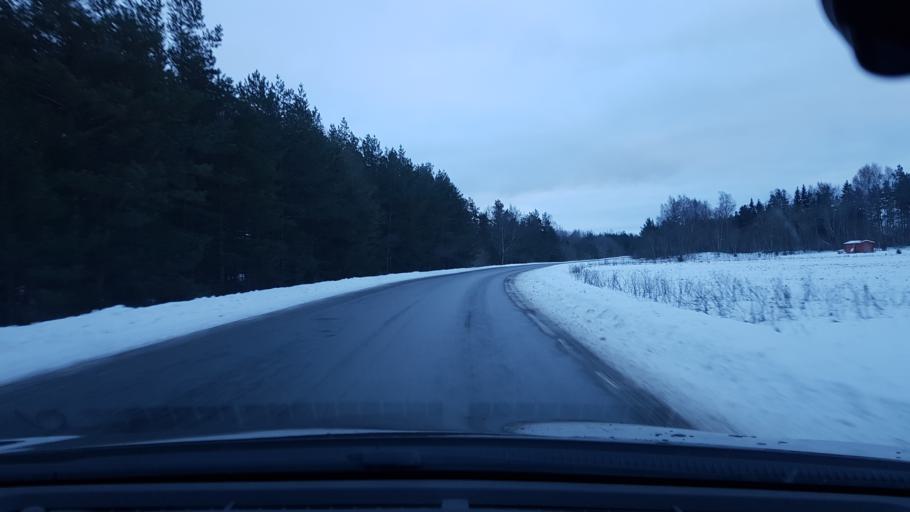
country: EE
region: Laeaene
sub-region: Ridala Parish
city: Uuemoisa
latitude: 59.0527
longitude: 23.6151
